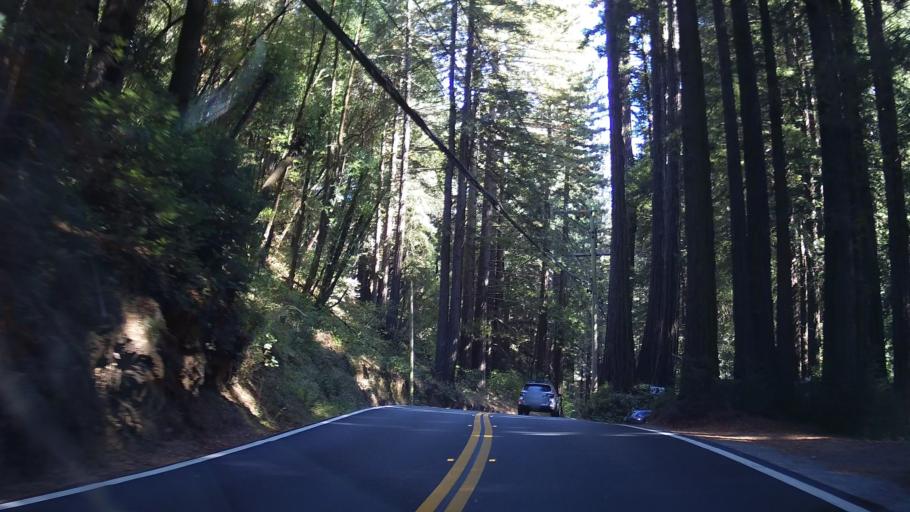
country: US
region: California
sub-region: Marin County
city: Lagunitas-Forest Knolls
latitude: 38.0513
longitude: -122.6848
